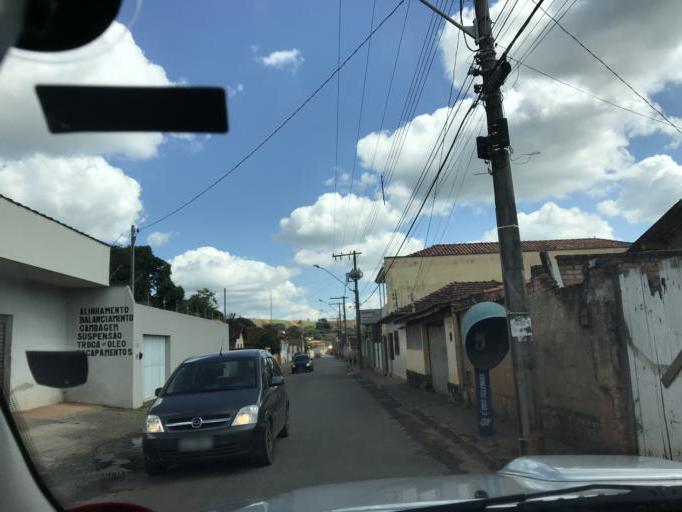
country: BR
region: Minas Gerais
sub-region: Campanha
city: Campanha
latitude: -21.8330
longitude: -45.4034
